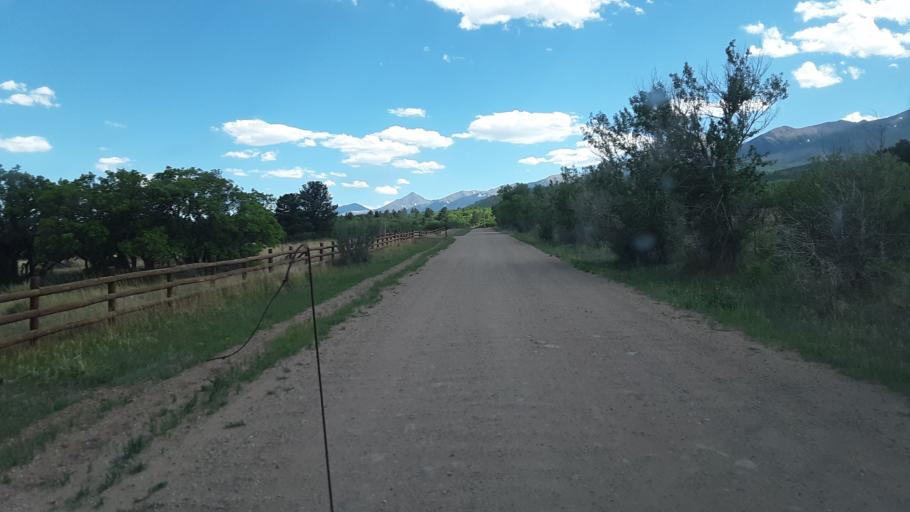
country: US
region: Colorado
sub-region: Custer County
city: Westcliffe
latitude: 38.2285
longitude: -105.5991
